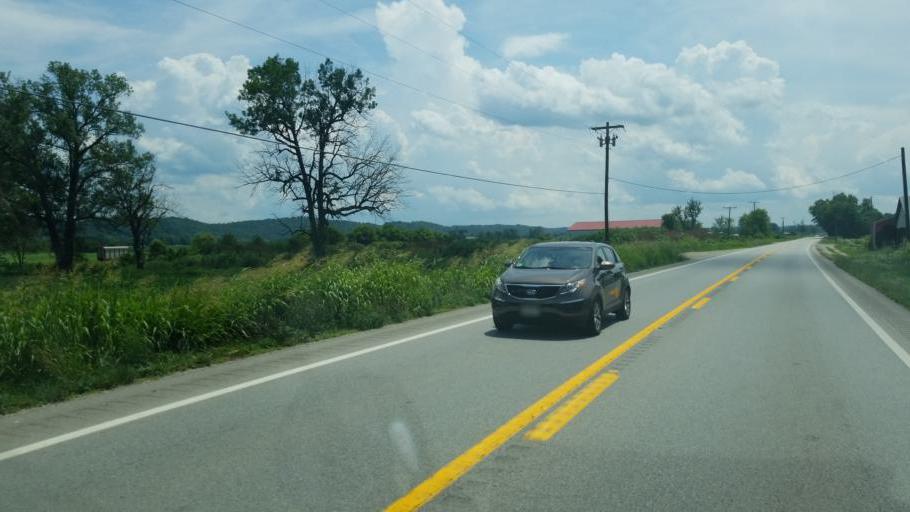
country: US
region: West Virginia
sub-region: Putnam County
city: Buffalo
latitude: 38.7128
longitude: -81.9678
